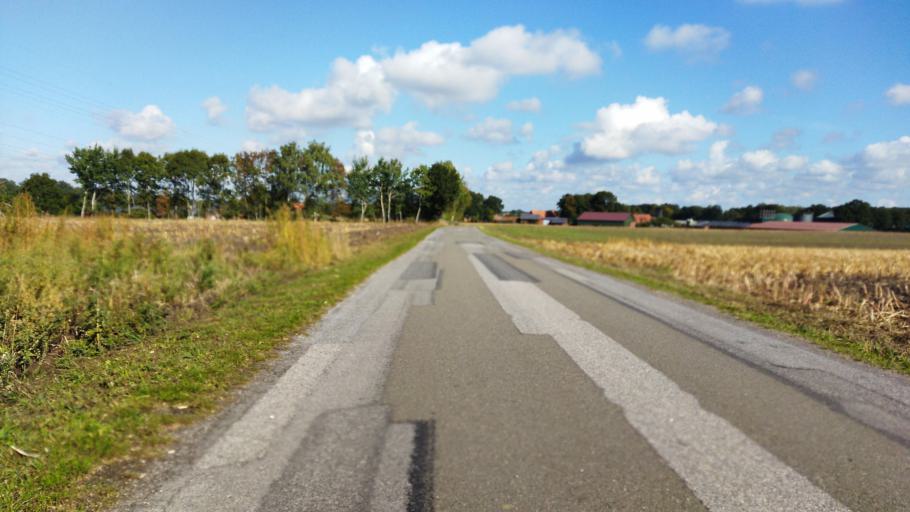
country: DE
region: Lower Saxony
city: Salzbergen
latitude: 52.3052
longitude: 7.3237
